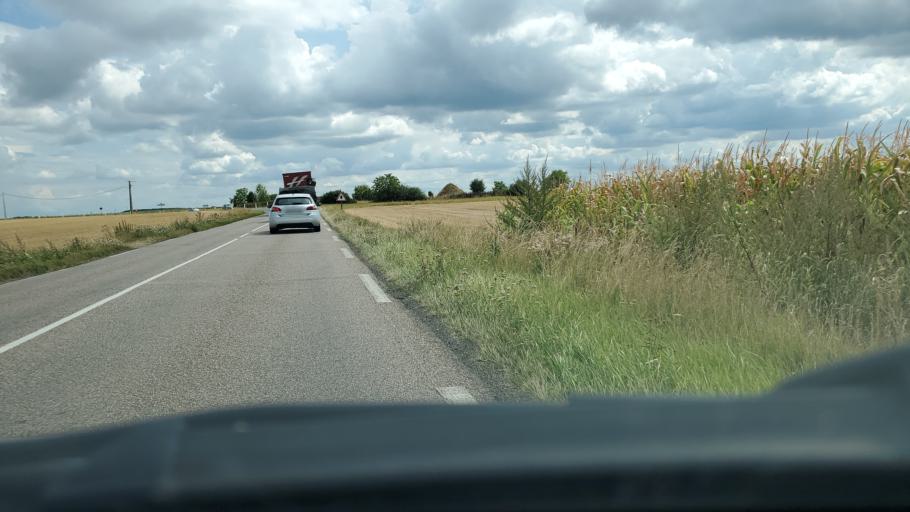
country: FR
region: Ile-de-France
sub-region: Departement de Seine-et-Marne
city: Bouleurs
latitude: 48.8939
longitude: 2.9419
